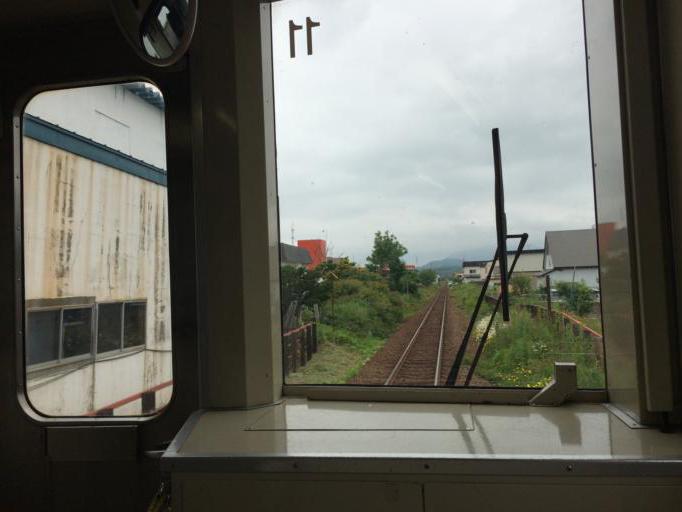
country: JP
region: Hokkaido
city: Yoichi
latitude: 43.1917
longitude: 140.8031
